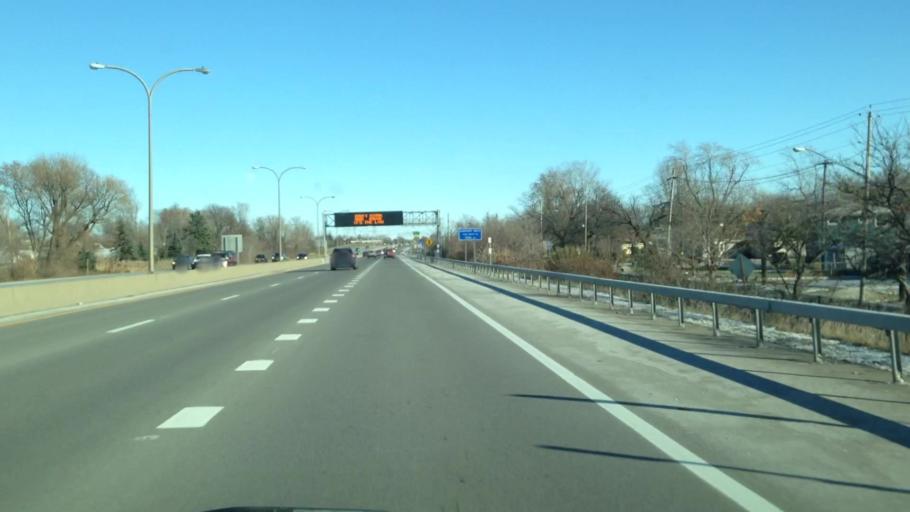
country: US
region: New York
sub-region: Erie County
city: Eggertsville
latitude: 42.9329
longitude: -78.7810
